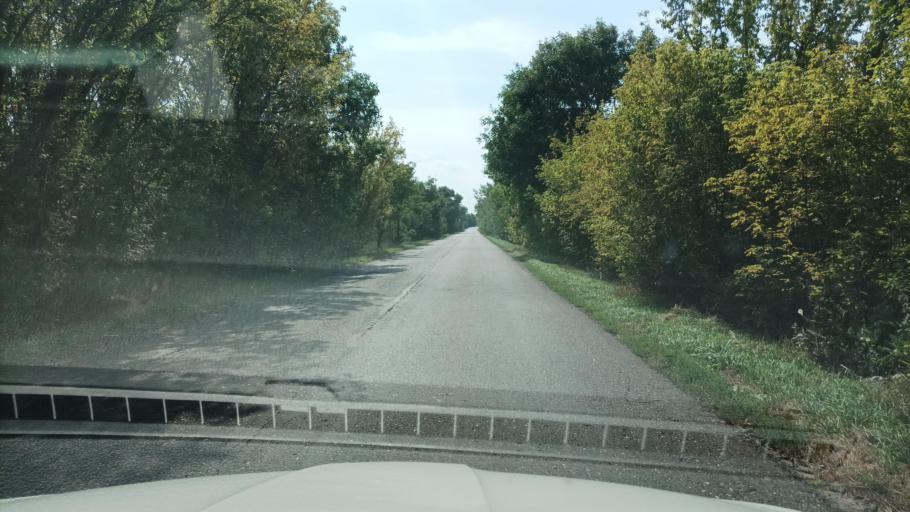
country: HU
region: Pest
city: Tura
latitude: 47.6409
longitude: 19.6404
